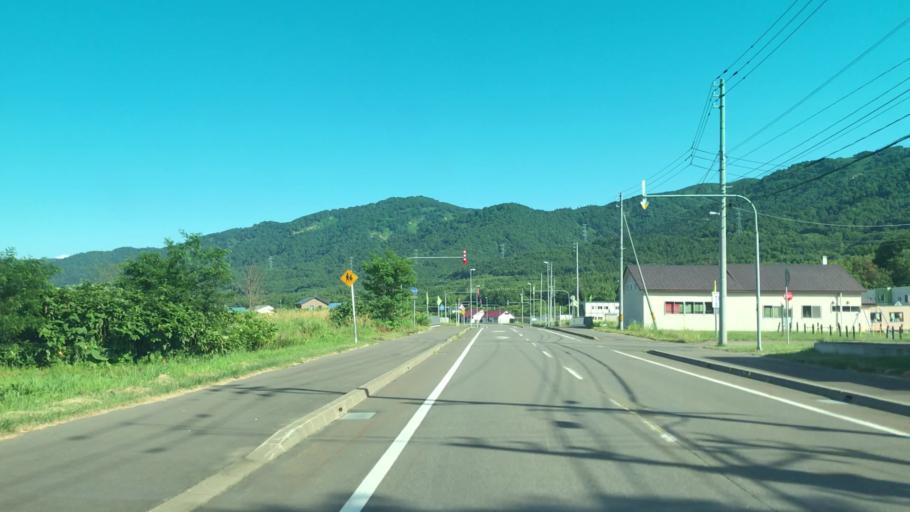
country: JP
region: Hokkaido
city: Yoichi
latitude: 43.0410
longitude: 140.7332
